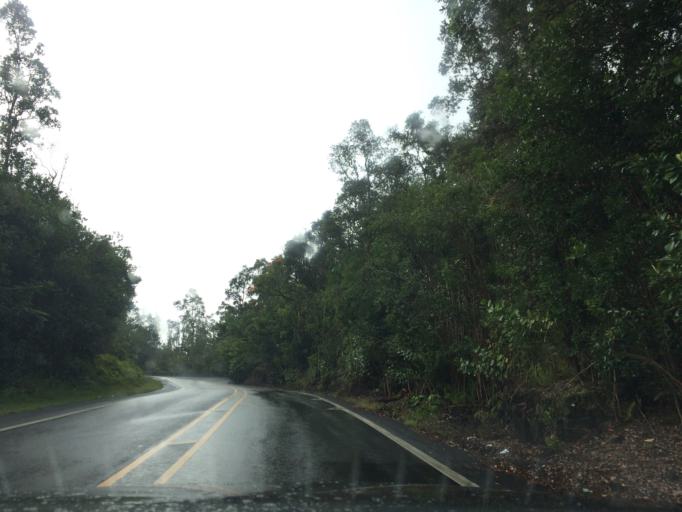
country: US
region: Hawaii
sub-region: Hawaii County
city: Hilo
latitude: 19.6880
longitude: -155.1297
